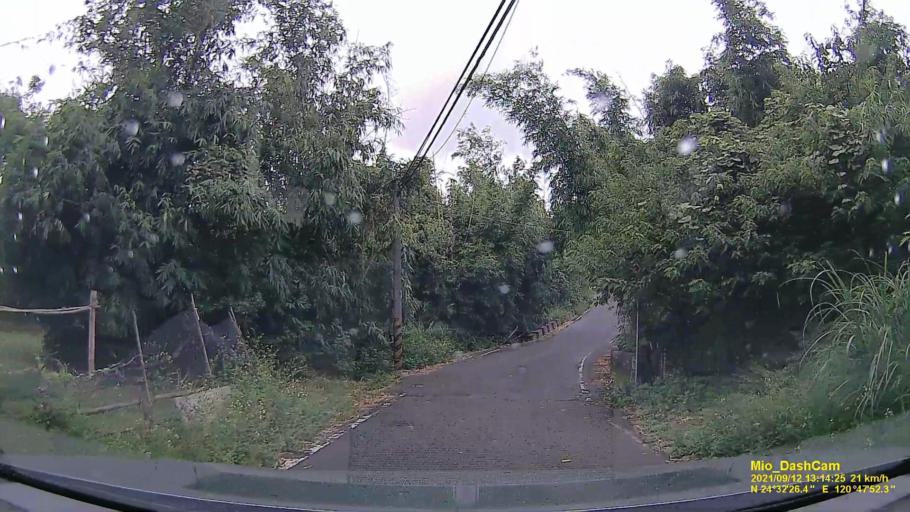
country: TW
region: Taiwan
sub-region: Miaoli
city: Miaoli
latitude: 24.5407
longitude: 120.7979
